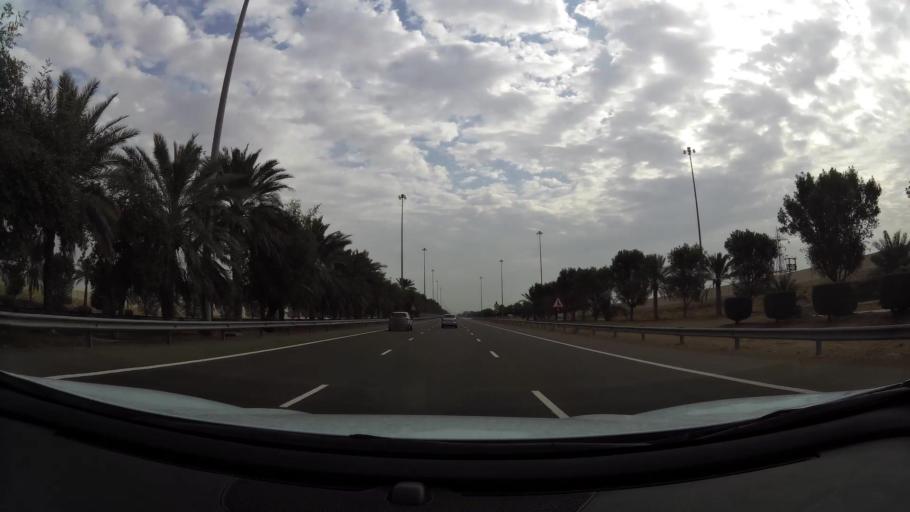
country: AE
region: Abu Dhabi
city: Al Ain
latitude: 24.2132
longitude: 55.5243
